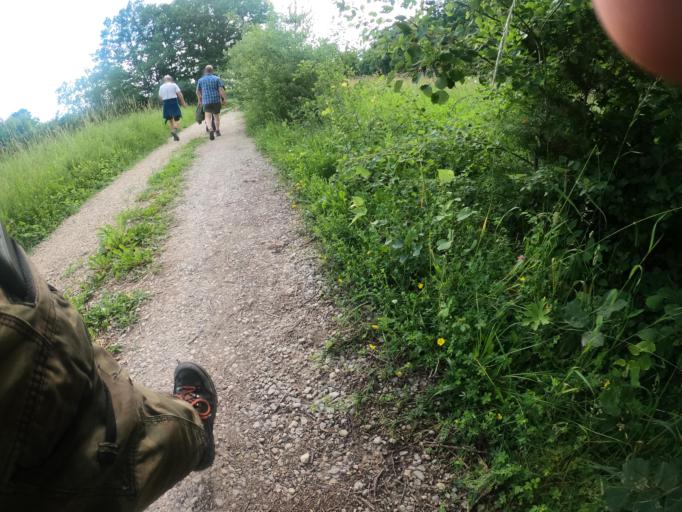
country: DE
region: Bavaria
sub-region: Upper Franconia
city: Memmelsdorf
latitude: 49.9256
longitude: 10.9671
